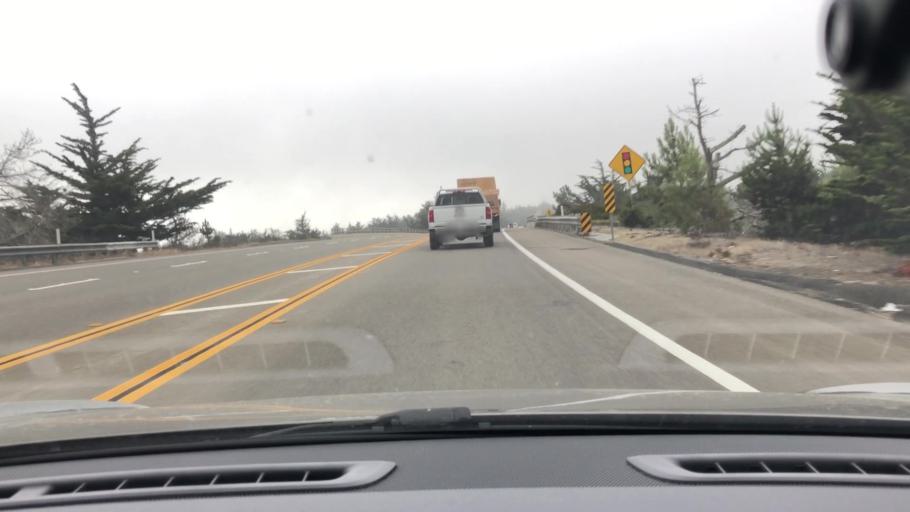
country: US
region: California
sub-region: Monterey County
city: Marina
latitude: 36.6472
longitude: -121.8168
